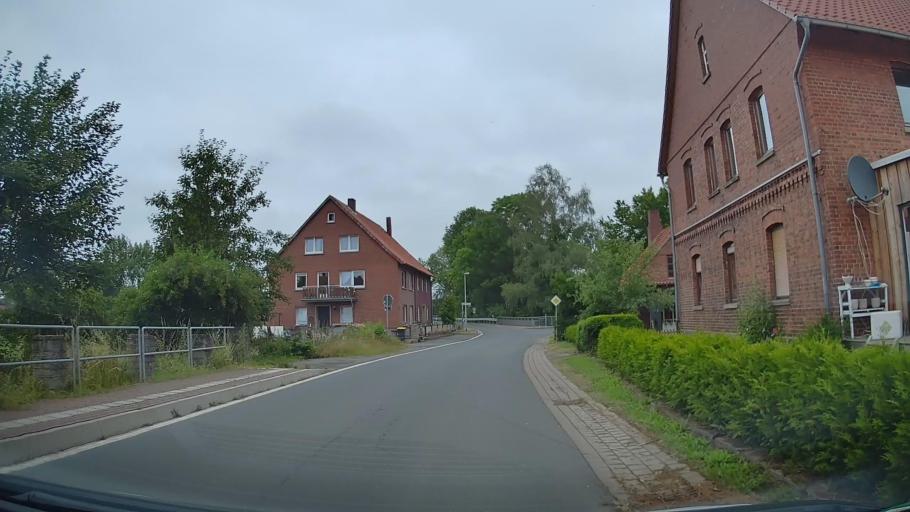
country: DE
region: Lower Saxony
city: Rinteln
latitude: 52.1537
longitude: 9.0959
